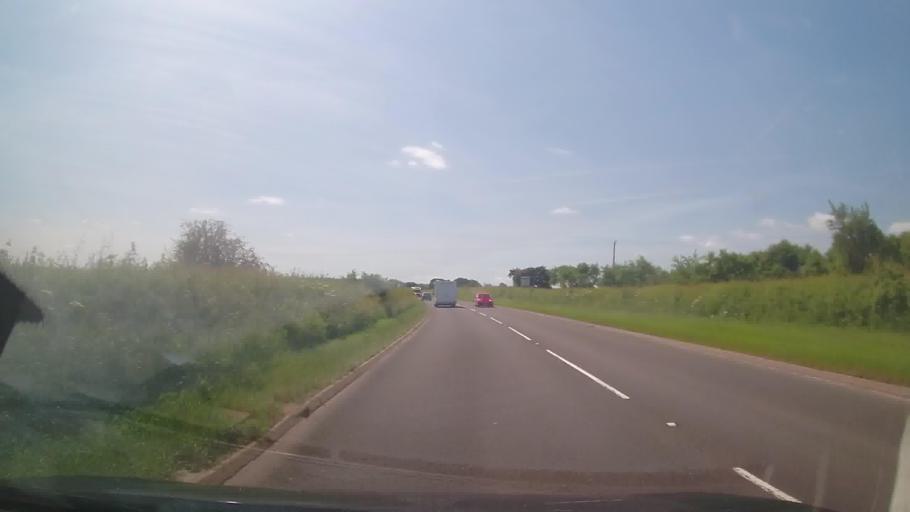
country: GB
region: England
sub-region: Herefordshire
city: Orleton
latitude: 52.3224
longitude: -2.7105
